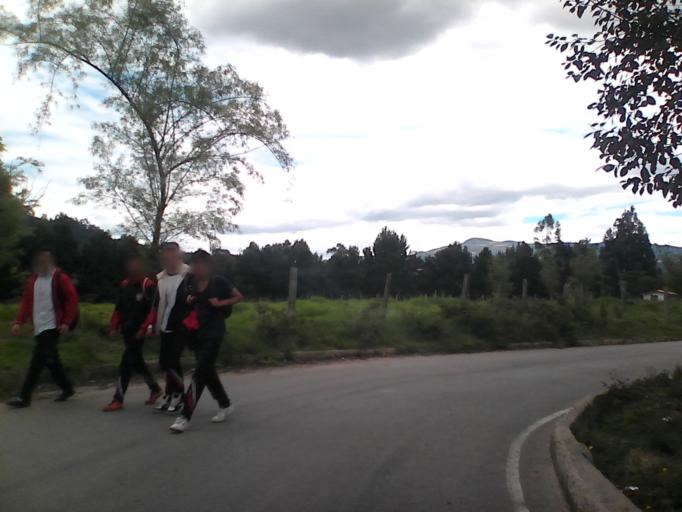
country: CO
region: Boyaca
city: Duitama
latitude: 5.8110
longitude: -73.0717
